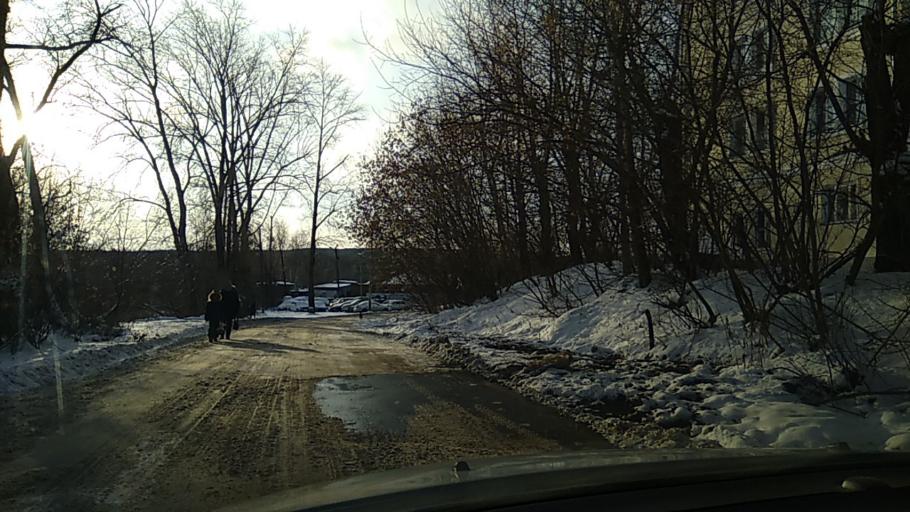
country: RU
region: Sverdlovsk
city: Shirokaya Rechka
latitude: 56.8468
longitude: 60.4989
